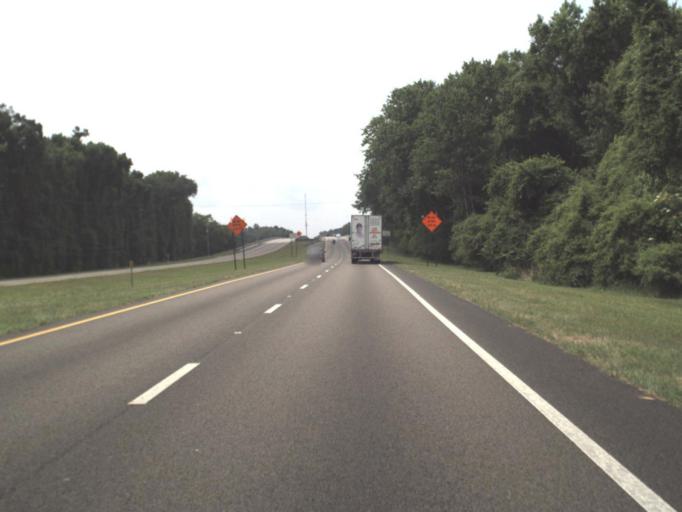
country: US
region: Florida
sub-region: Clay County
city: Green Cove Springs
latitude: 30.0464
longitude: -81.7086
